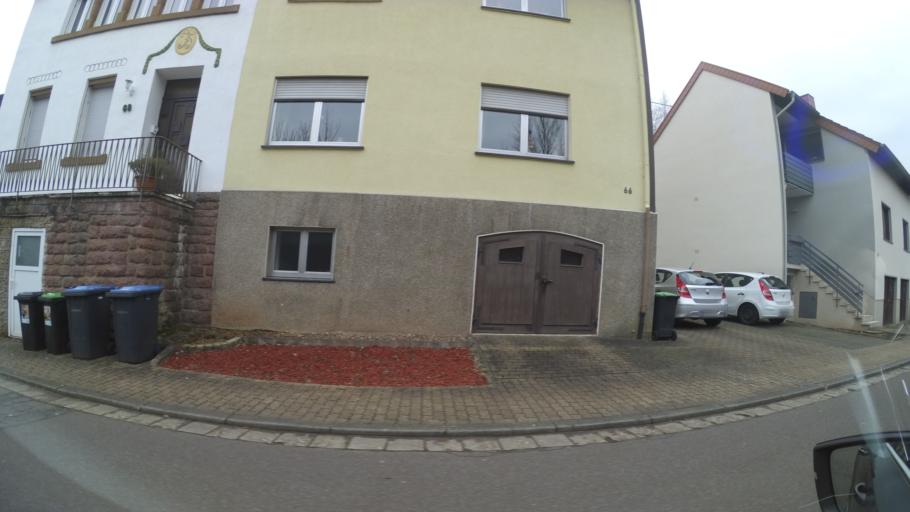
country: DE
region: Saarland
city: Illingen
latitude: 49.3820
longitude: 7.0732
